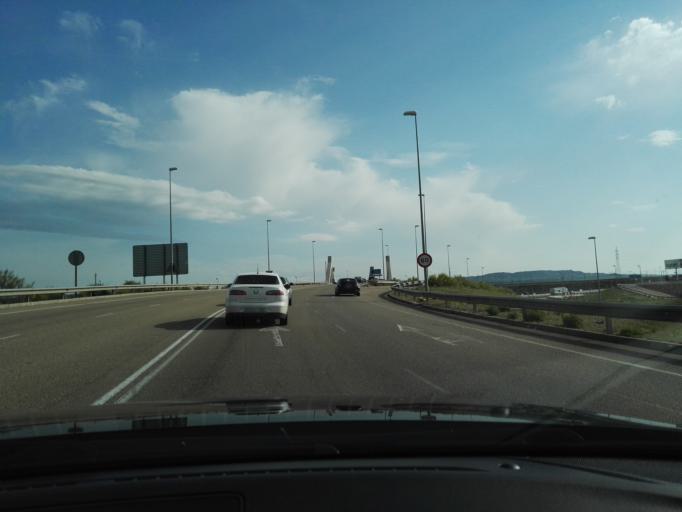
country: ES
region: Aragon
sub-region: Provincia de Zaragoza
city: Montecanal
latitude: 41.6322
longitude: -0.9888
